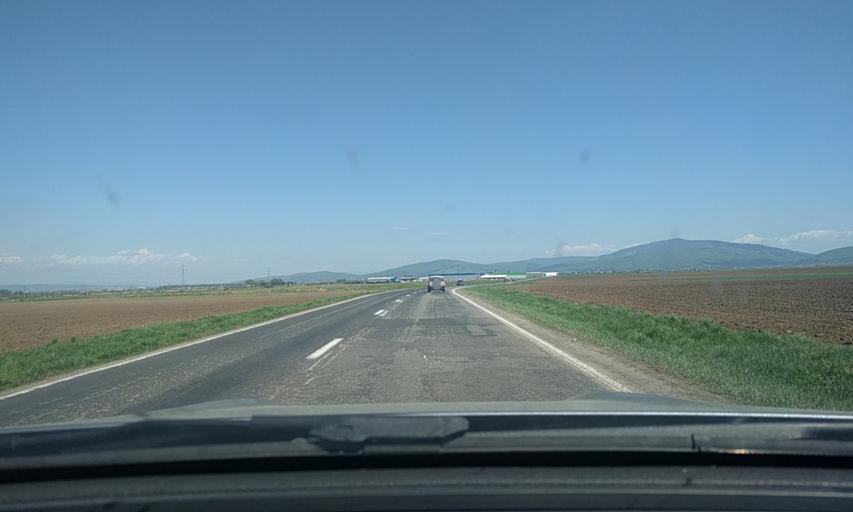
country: RO
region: Brasov
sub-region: Comuna Harman
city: Harman
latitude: 45.7131
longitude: 25.7216
